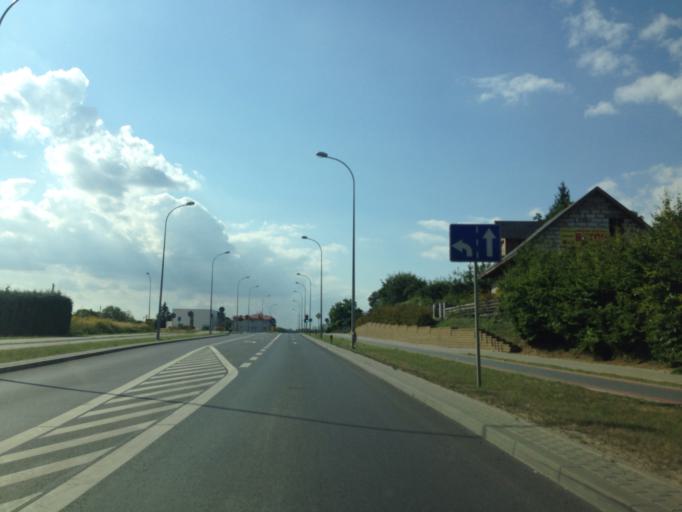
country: PL
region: Warmian-Masurian Voivodeship
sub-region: Powiat ilawski
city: Ilawa
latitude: 53.6010
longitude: 19.5684
